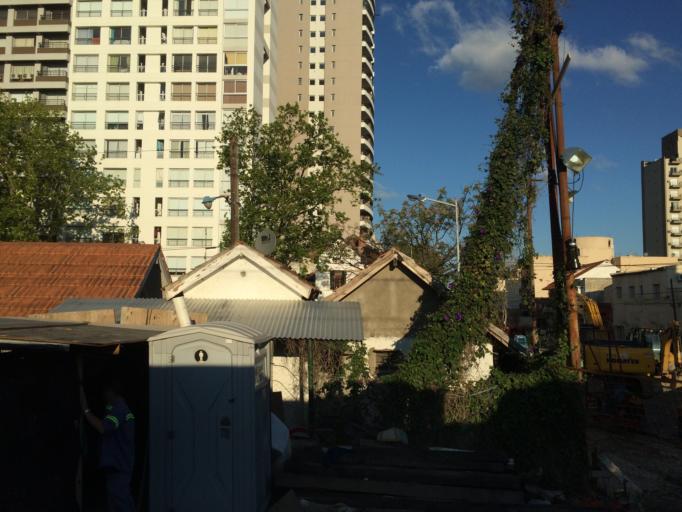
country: AR
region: Buenos Aires
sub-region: Partido de Lomas de Zamora
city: Lomas de Zamora
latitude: -34.7454
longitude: -58.3954
